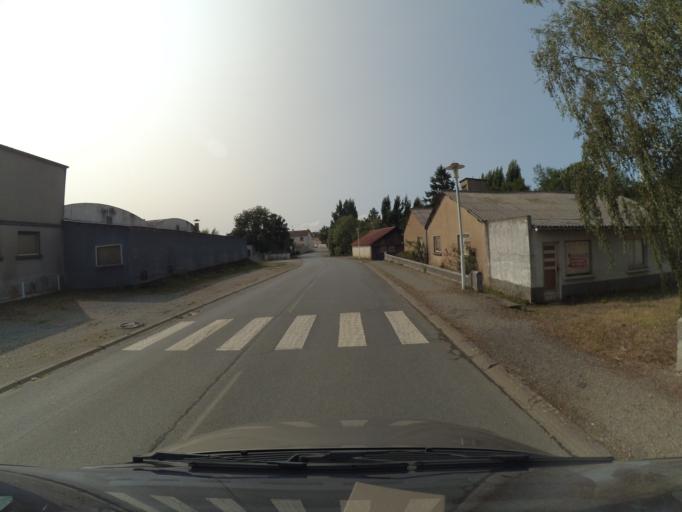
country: FR
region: Pays de la Loire
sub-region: Departement de la Vendee
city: Treize-Septiers
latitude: 46.9831
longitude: -1.2274
